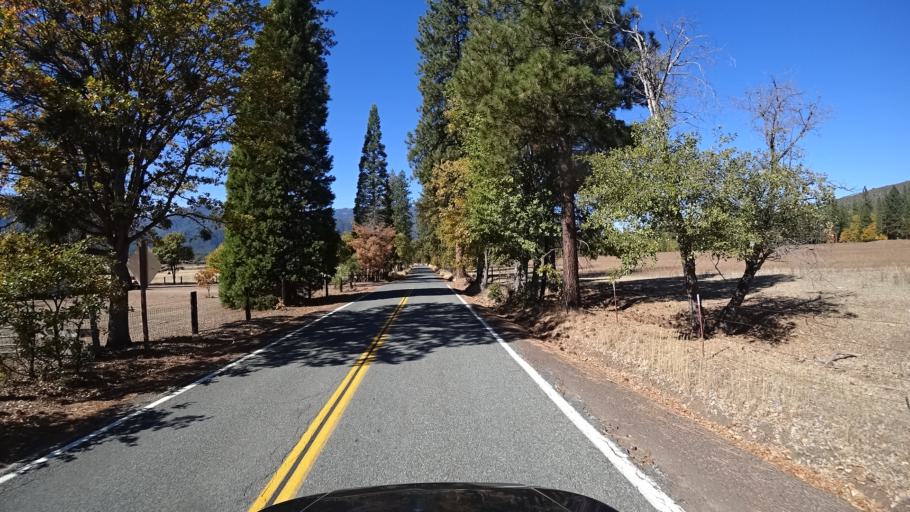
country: US
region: California
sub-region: Siskiyou County
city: Yreka
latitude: 41.5711
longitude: -122.9431
